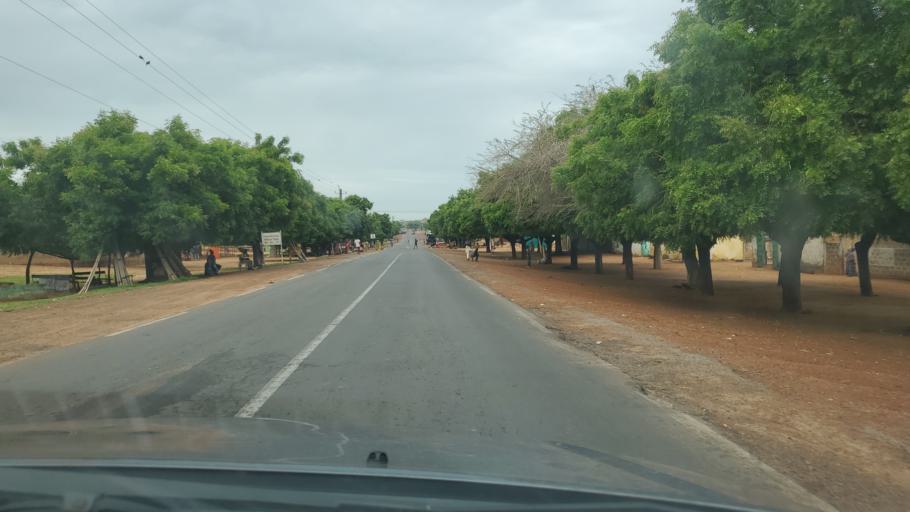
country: SN
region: Thies
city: Mekhe
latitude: 15.1308
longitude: -16.8598
